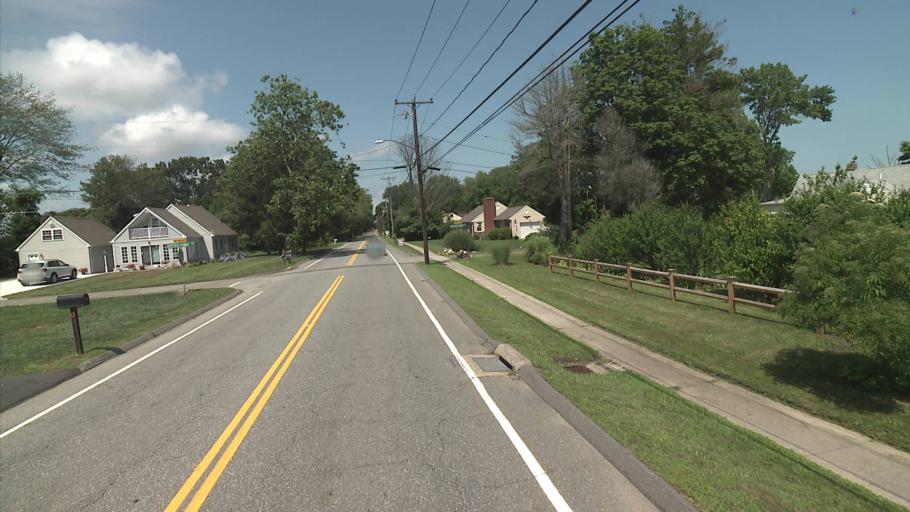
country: US
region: Connecticut
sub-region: Middlesex County
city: Saybrook Manor
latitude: 41.2801
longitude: -72.3923
